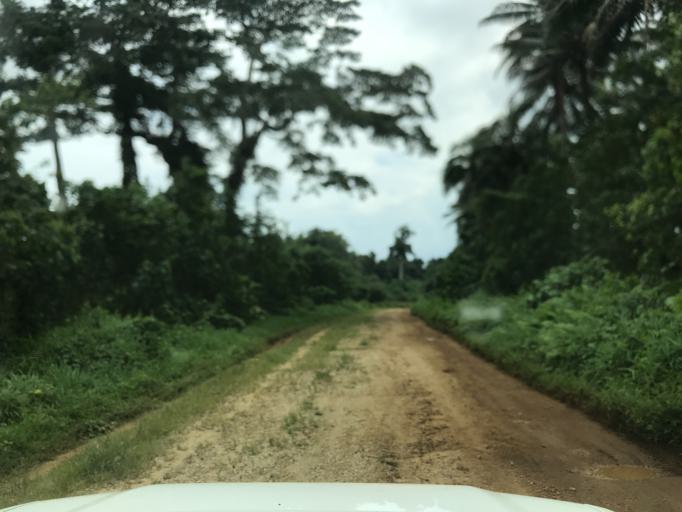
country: VU
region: Sanma
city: Port-Olry
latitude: -15.1870
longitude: 167.0152
